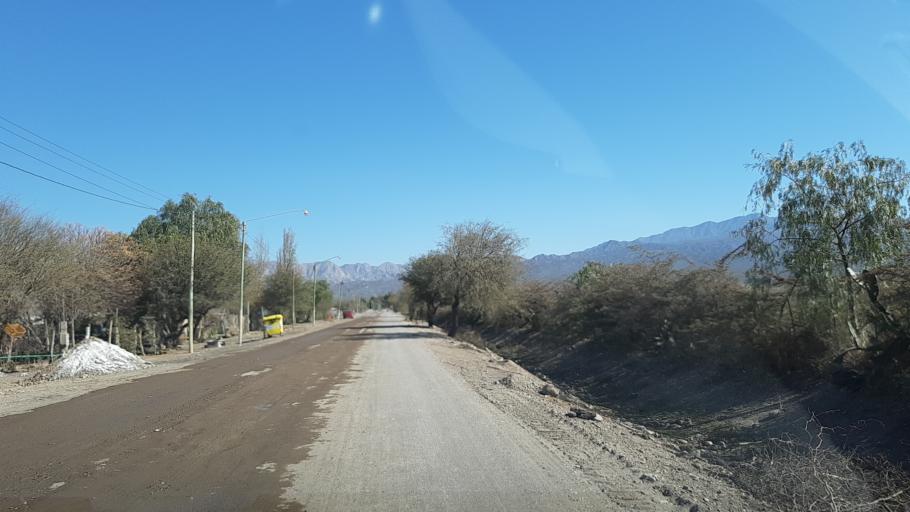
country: AR
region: San Juan
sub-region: Departamento de Zonda
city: Zonda
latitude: -31.4691
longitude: -68.7231
